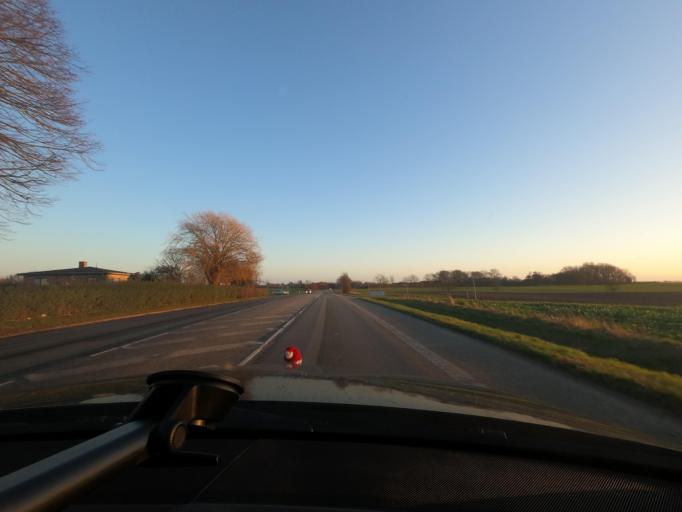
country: DK
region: South Denmark
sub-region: Sonderborg Kommune
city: Horuphav
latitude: 54.8956
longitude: 9.9653
